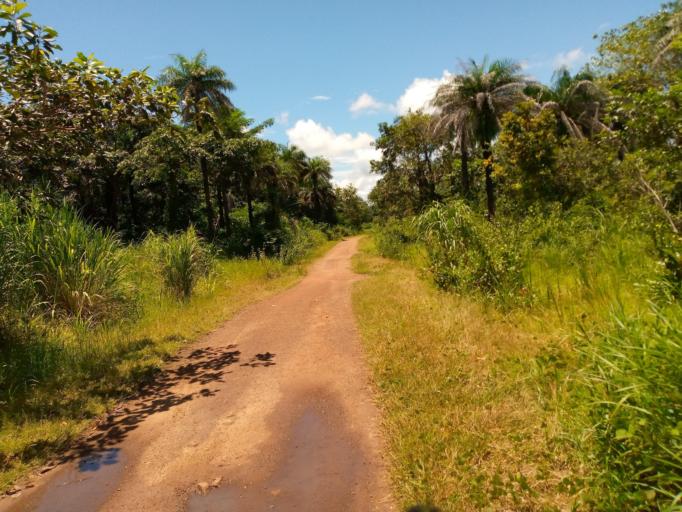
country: SL
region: Northern Province
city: Binkolo
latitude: 9.1032
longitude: -12.1408
